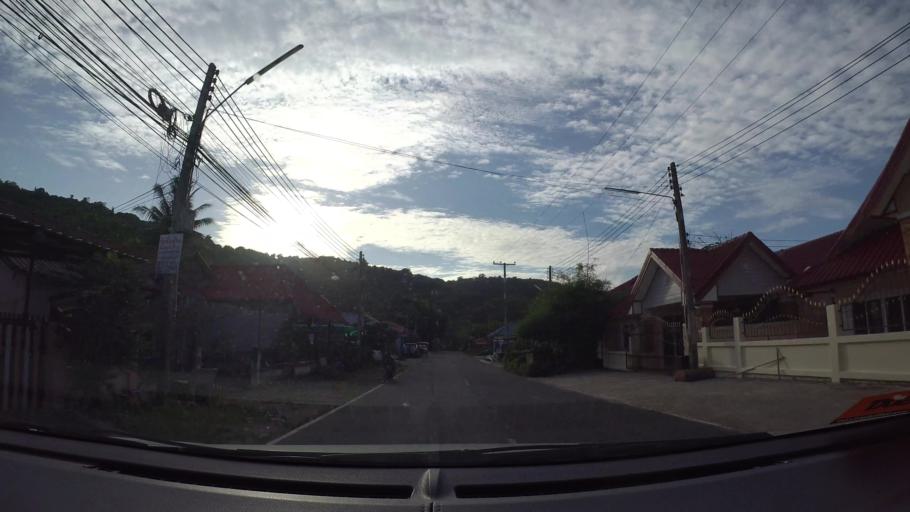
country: TH
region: Chon Buri
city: Sattahip
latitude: 12.6913
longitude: 100.9253
